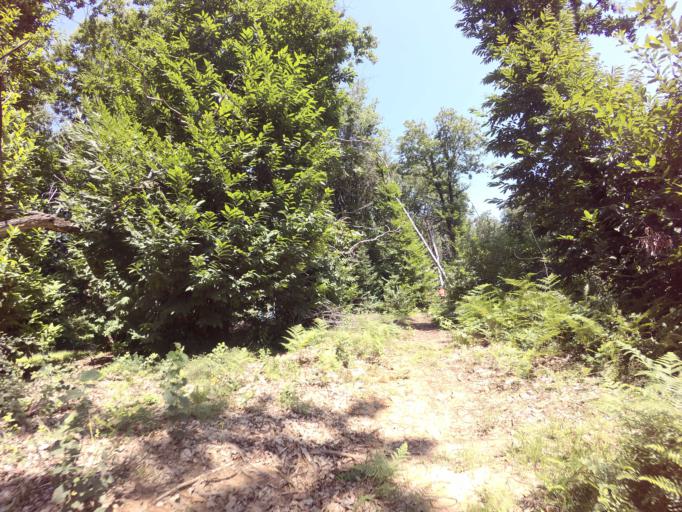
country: IT
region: Piedmont
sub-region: Provincia di Cuneo
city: Pianfei
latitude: 44.3387
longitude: 7.7061
